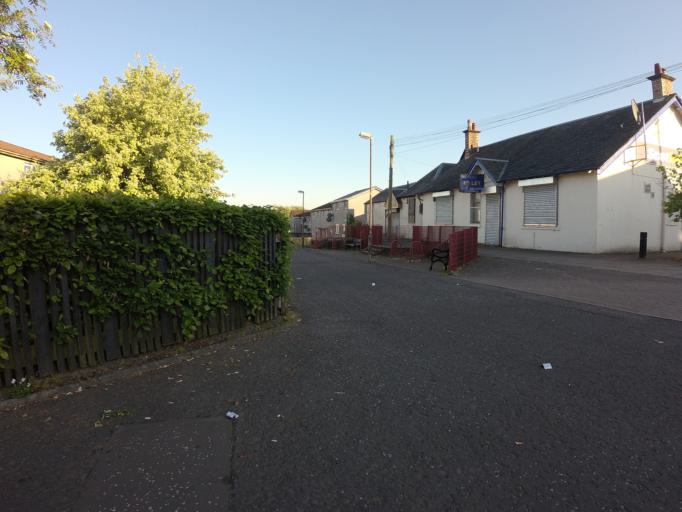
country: GB
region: Scotland
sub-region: West Lothian
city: Livingston
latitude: 55.9003
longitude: -3.5660
